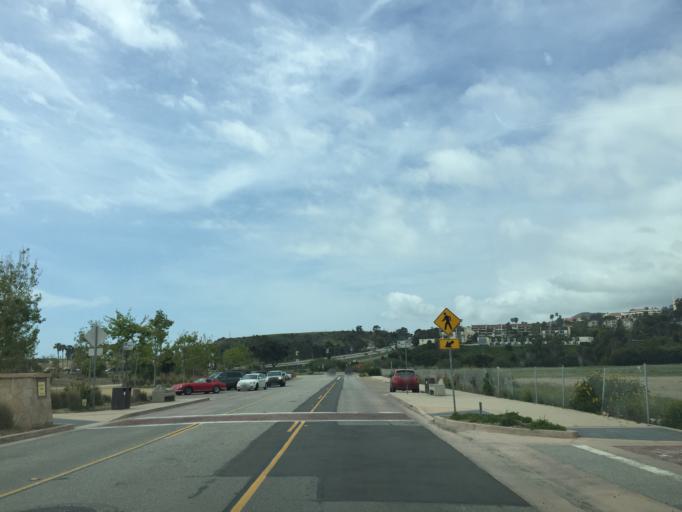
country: US
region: California
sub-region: Los Angeles County
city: Malibu Beach
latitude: 34.0362
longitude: -118.6900
